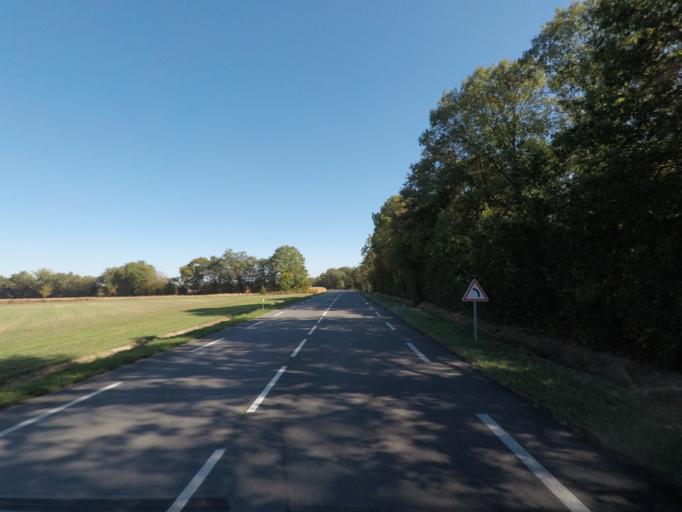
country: FR
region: Rhone-Alpes
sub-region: Departement de l'Ain
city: Servas
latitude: 46.1144
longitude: 5.1504
